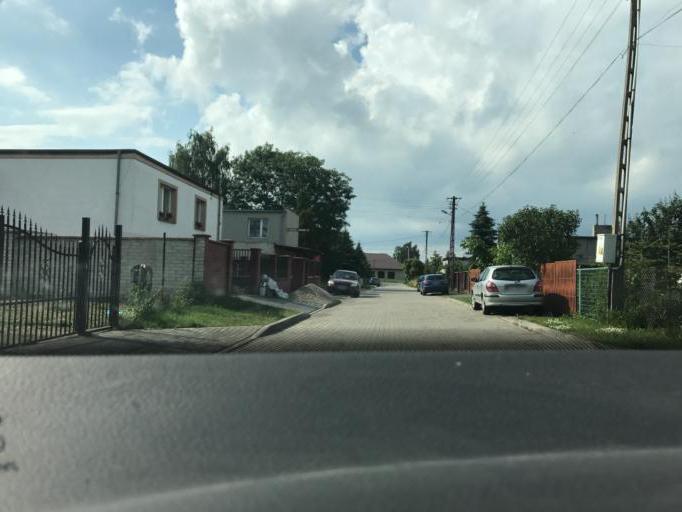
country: PL
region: Pomeranian Voivodeship
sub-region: Powiat gdanski
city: Cedry Wielkie
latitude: 54.3356
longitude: 18.8002
